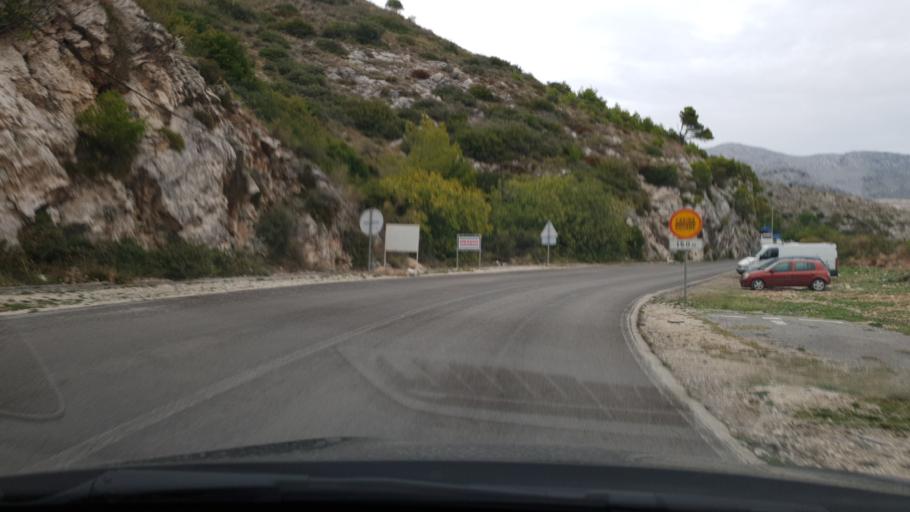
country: HR
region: Dubrovacko-Neretvanska
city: Cibaca
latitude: 42.6551
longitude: 18.1590
